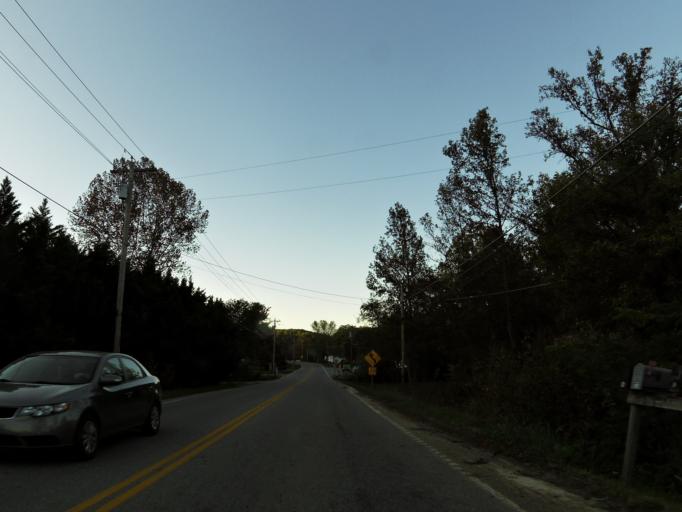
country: US
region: Tennessee
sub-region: Anderson County
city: Rocky Top
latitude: 36.2471
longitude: -84.1674
